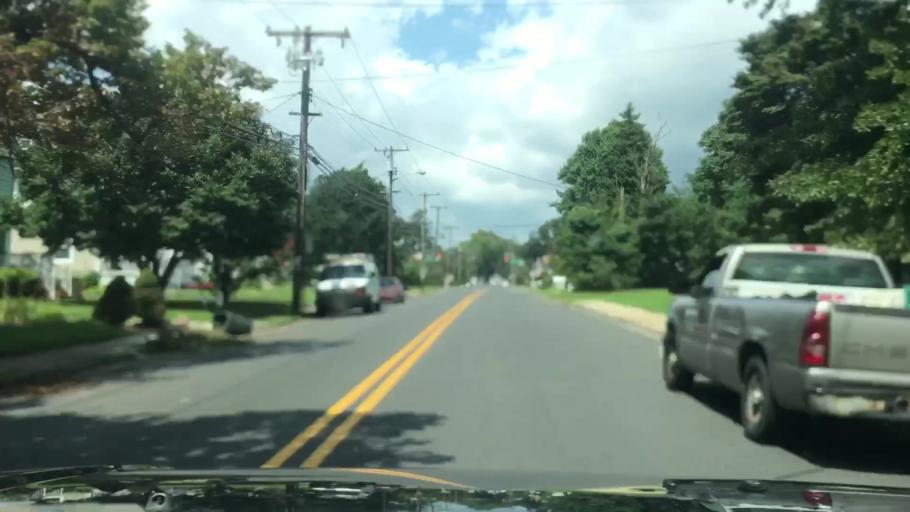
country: US
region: New Jersey
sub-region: Monmouth County
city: Long Branch
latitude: 40.3105
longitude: -73.9877
